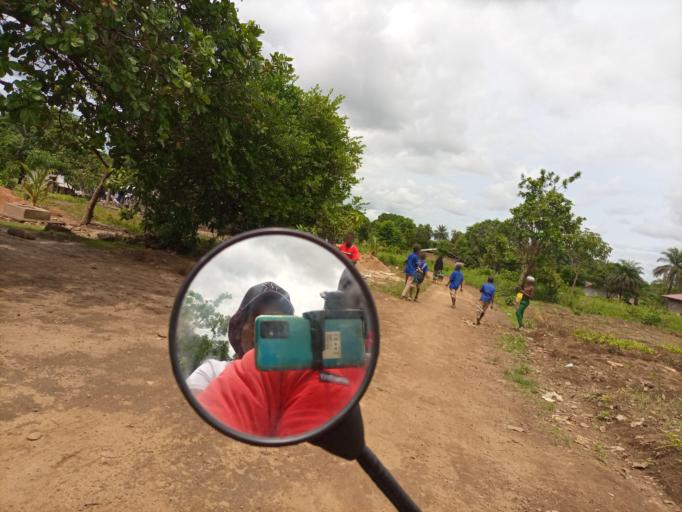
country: SL
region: Southern Province
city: Bo
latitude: 7.9686
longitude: -11.7156
